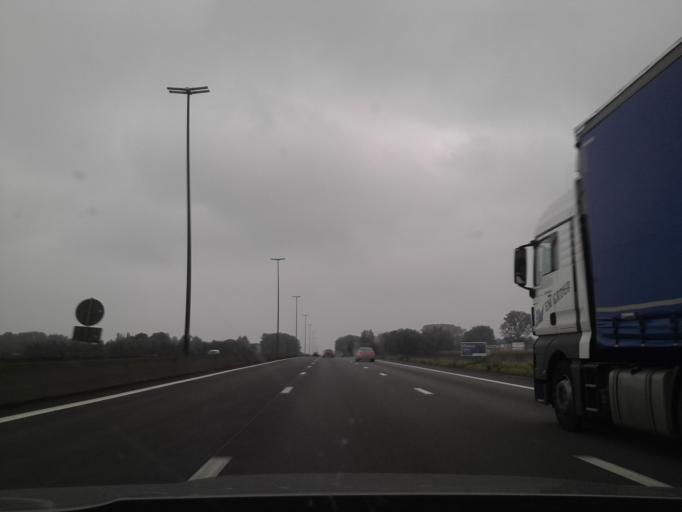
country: BE
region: Wallonia
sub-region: Province du Hainaut
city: Roeulx
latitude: 50.4816
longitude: 4.0449
